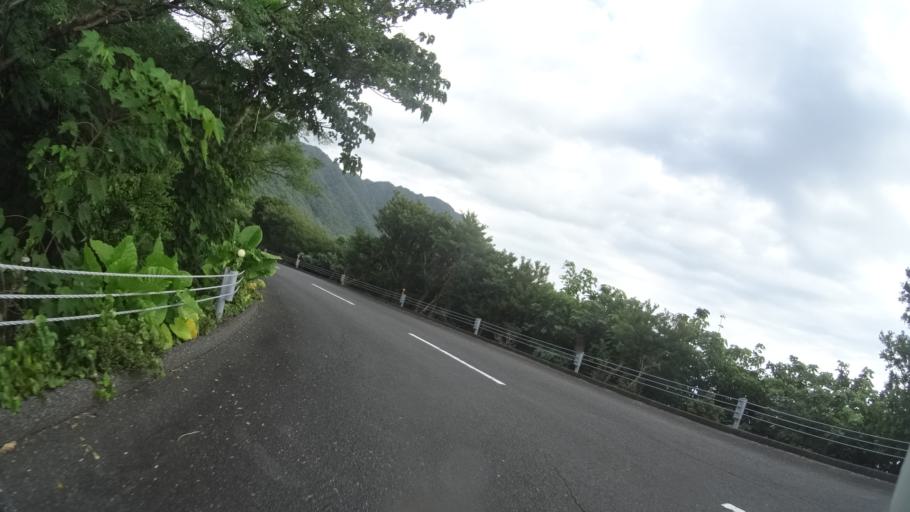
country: JP
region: Kagoshima
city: Nishinoomote
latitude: 30.3188
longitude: 130.3982
